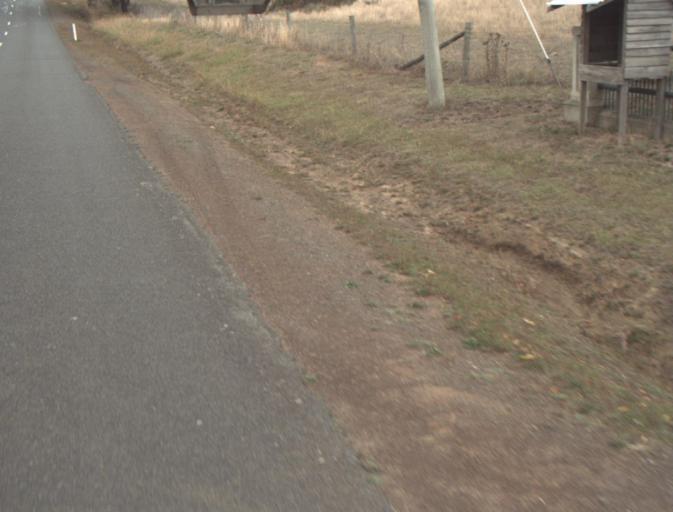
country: AU
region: Tasmania
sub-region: Launceston
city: Summerhill
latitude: -41.4990
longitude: 147.1879
